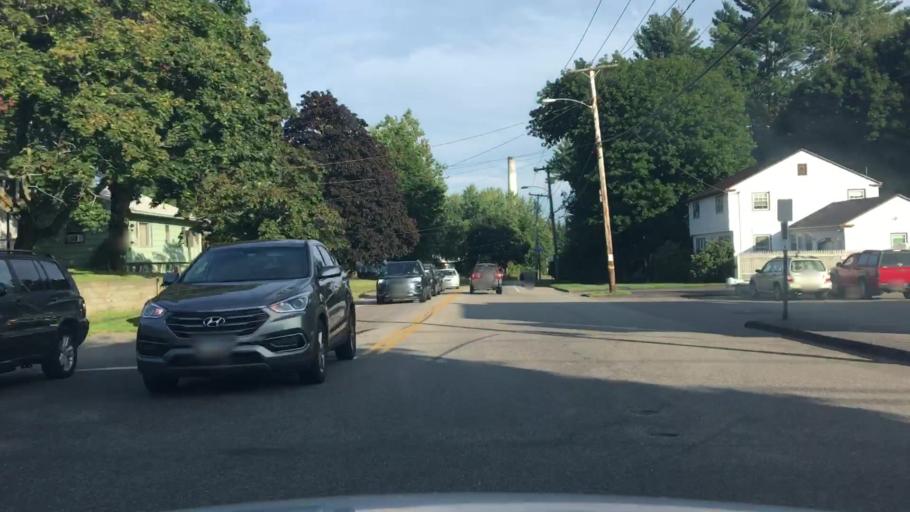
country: US
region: Maine
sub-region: Cumberland County
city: Westbrook
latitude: 43.6886
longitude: -70.3610
